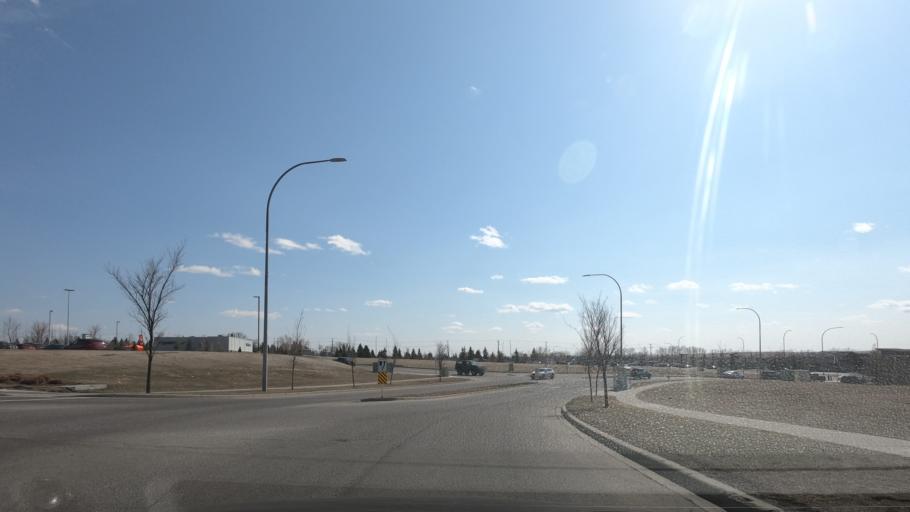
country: CA
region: Alberta
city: Airdrie
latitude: 51.3022
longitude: -114.0113
